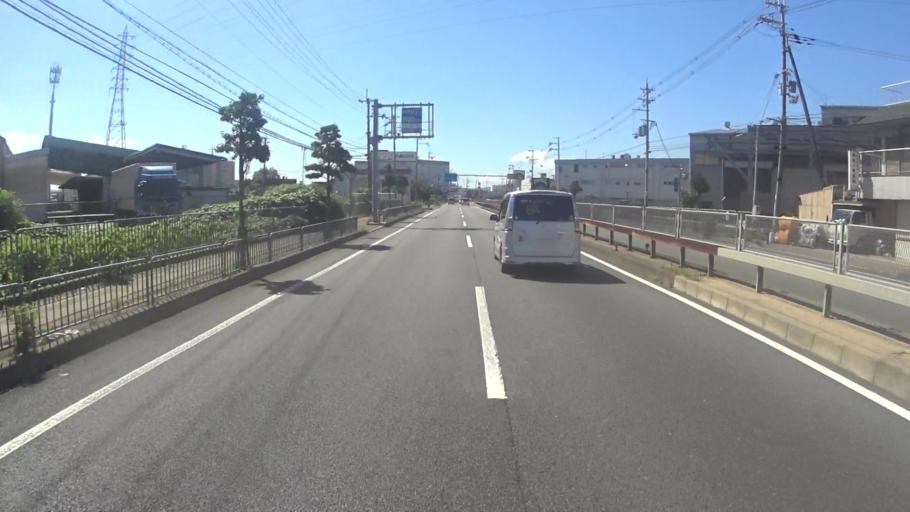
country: JP
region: Kyoto
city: Yawata
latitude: 34.8933
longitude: 135.7440
